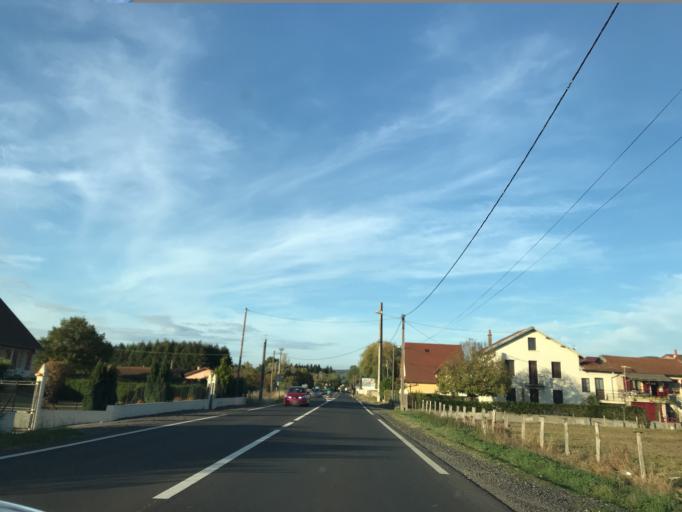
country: FR
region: Auvergne
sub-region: Departement du Puy-de-Dome
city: Puy-Guillaume
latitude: 46.0045
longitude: 3.4862
